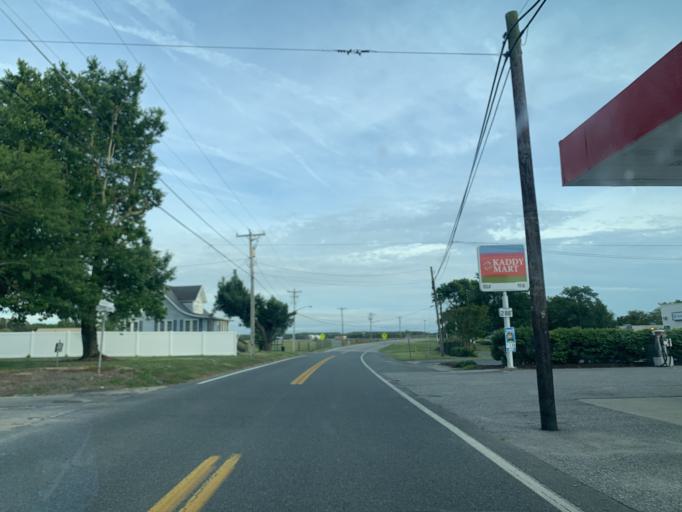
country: US
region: Maryland
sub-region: Worcester County
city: Snow Hill
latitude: 38.1693
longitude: -75.4003
